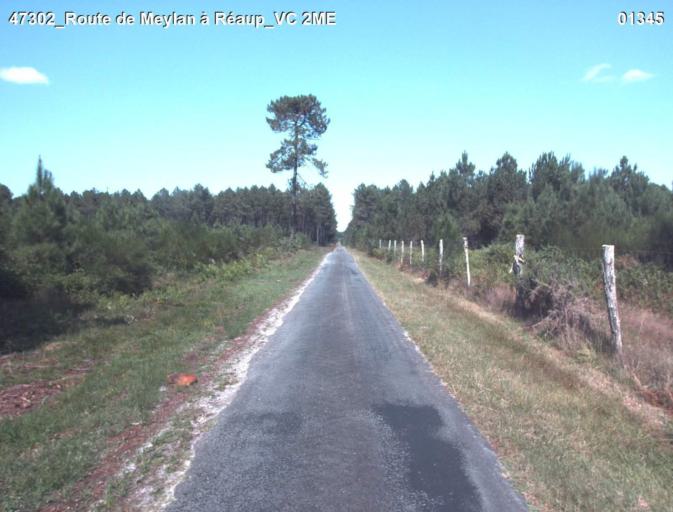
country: FR
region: Aquitaine
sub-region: Departement du Lot-et-Garonne
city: Mezin
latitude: 44.0970
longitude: 0.1331
